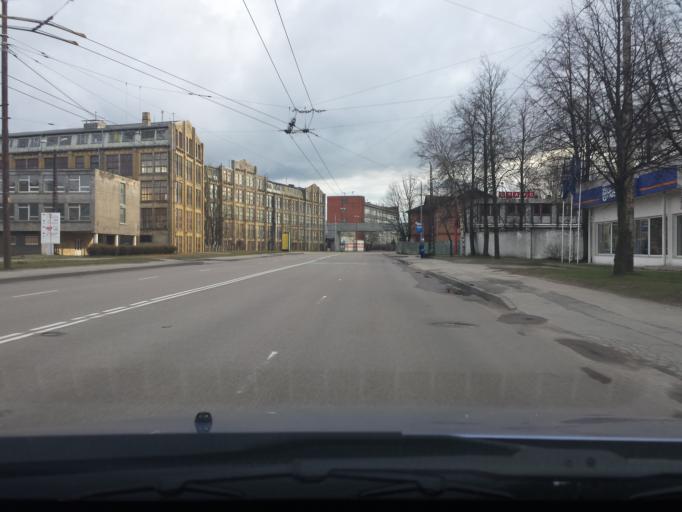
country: LV
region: Riga
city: Riga
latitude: 56.9873
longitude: 24.1212
